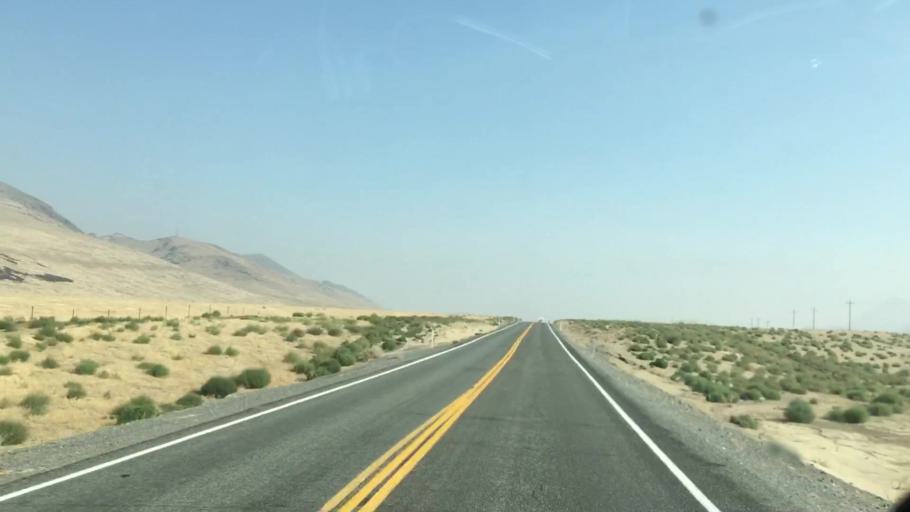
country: US
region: Nevada
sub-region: Lyon County
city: Fernley
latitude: 40.3833
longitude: -119.3331
